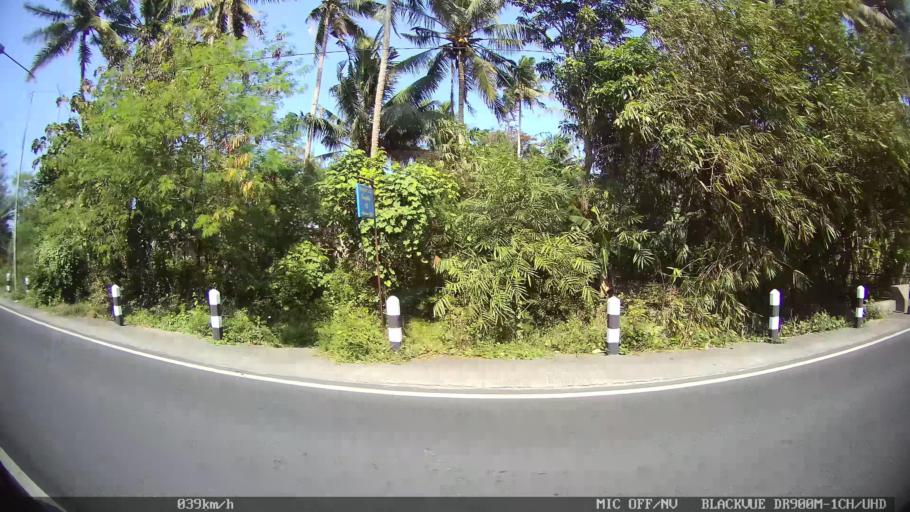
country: ID
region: Daerah Istimewa Yogyakarta
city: Srandakan
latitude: -7.9388
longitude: 110.2248
